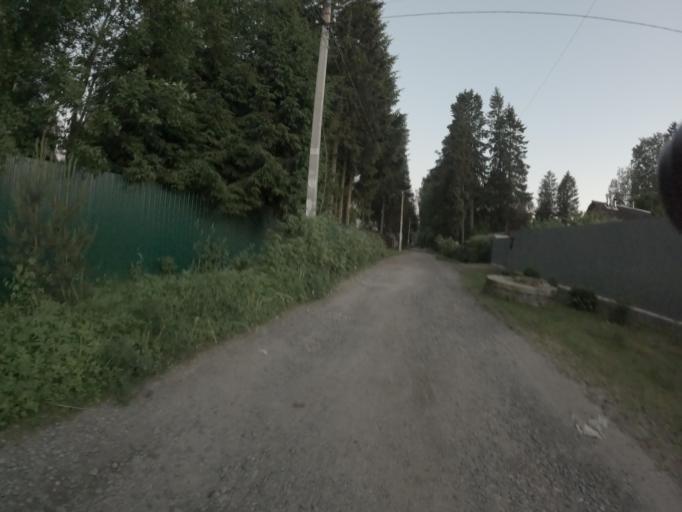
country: RU
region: Leningrad
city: Vsevolozhsk
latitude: 60.0177
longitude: 30.6163
